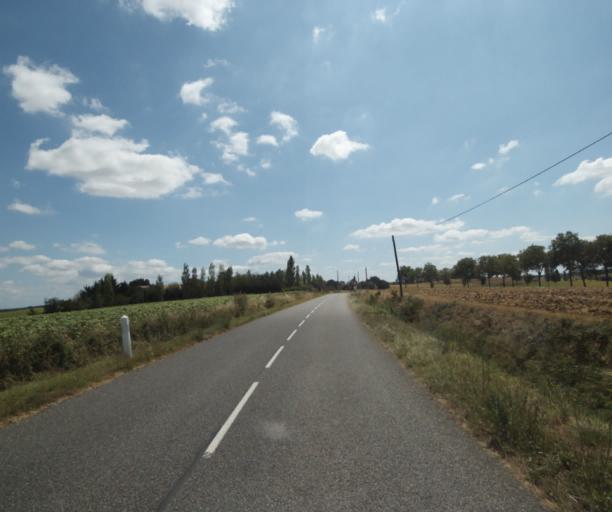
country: FR
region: Midi-Pyrenees
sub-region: Departement de la Haute-Garonne
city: Auriac-sur-Vendinelle
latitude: 43.4630
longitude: 1.8276
